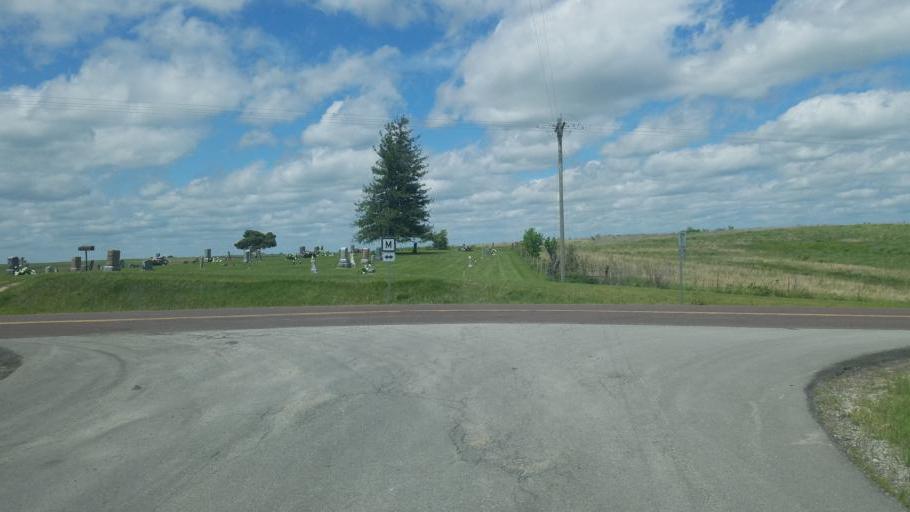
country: US
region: Iowa
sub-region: Decatur County
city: Lamoni
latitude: 40.4711
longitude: -94.0687
